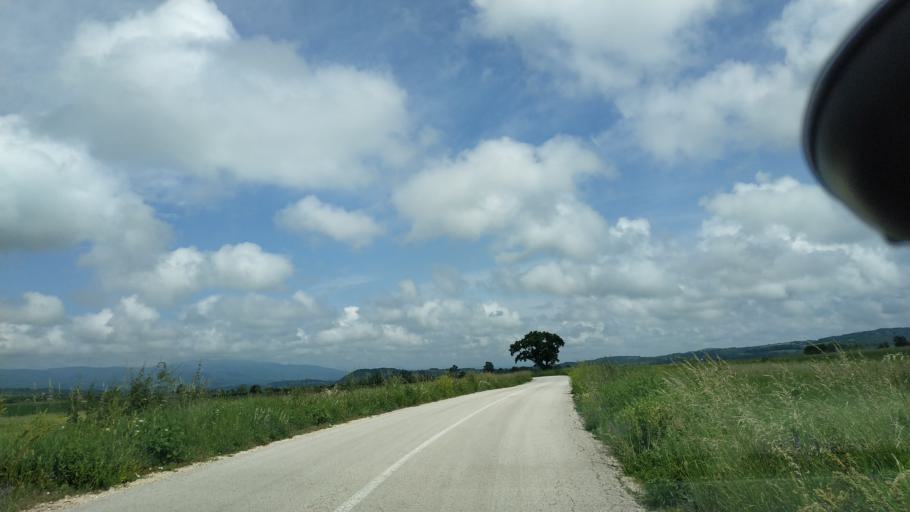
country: RS
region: Central Serbia
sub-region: Zajecarski Okrug
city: Boljevac
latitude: 43.8087
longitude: 21.9552
